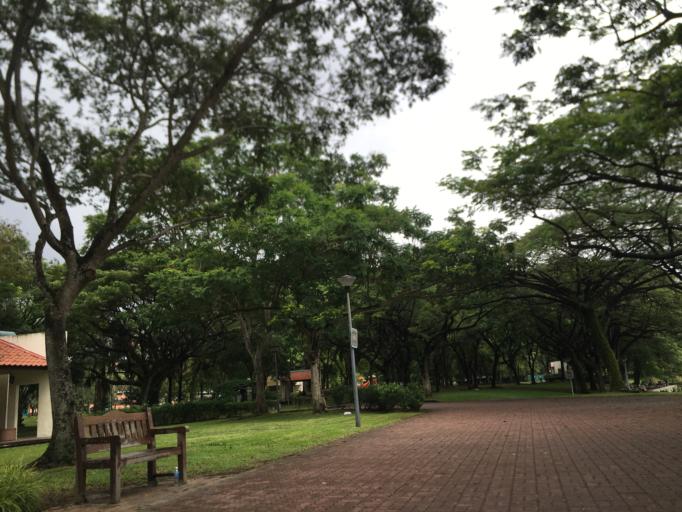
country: MY
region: Johor
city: Kampung Pasir Gudang Baru
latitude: 1.3764
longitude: 103.8978
